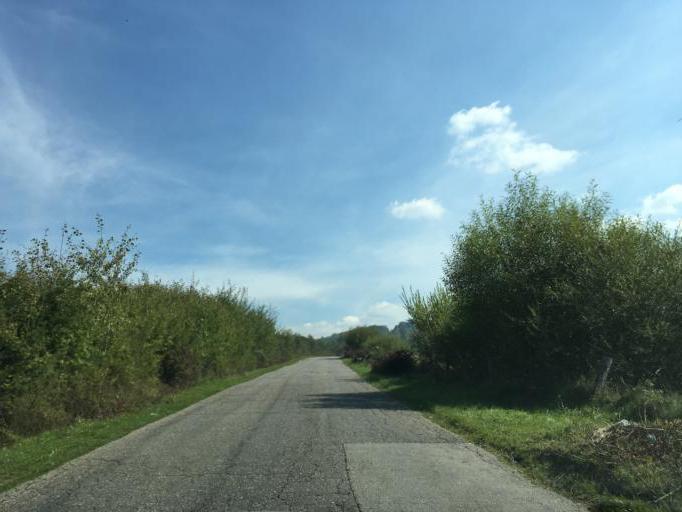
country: BA
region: Federation of Bosnia and Herzegovina
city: Bugojno
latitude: 44.0577
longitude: 17.4683
